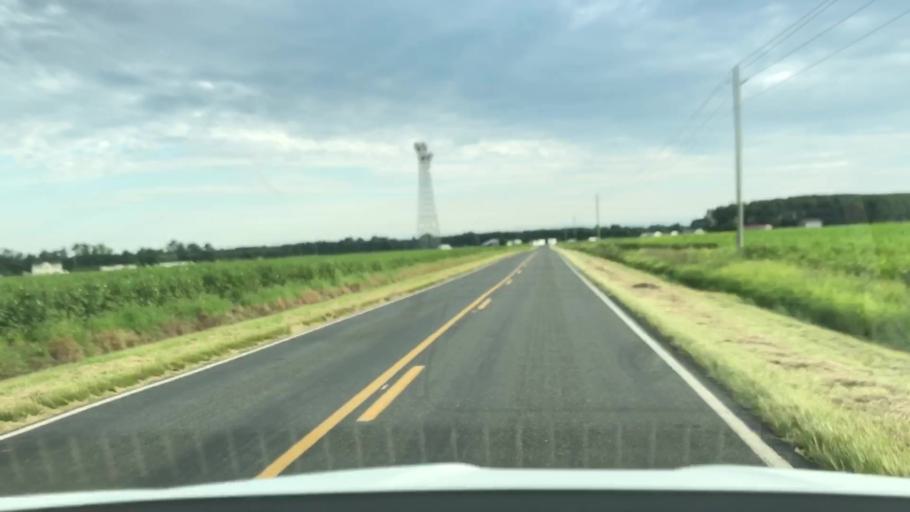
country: US
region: North Carolina
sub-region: Jones County
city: Maysville
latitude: 34.9912
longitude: -77.2806
